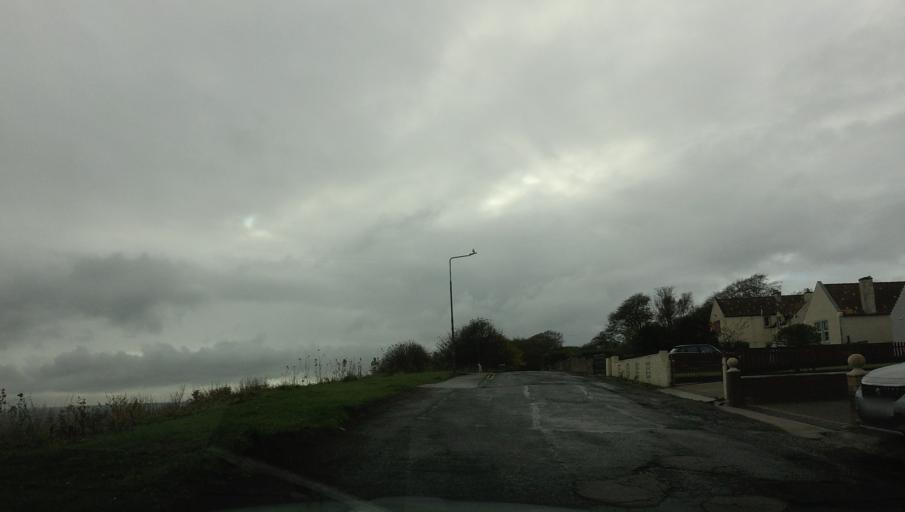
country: GB
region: Scotland
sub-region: Fife
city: East Wemyss
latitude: 56.1545
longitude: -3.0705
